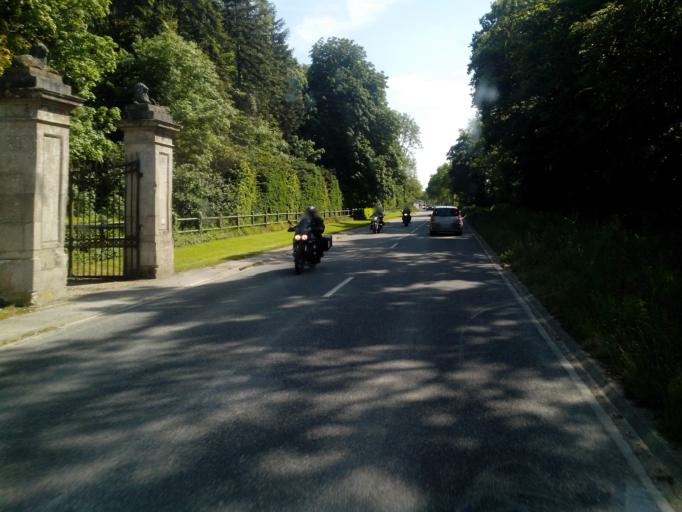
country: FR
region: Picardie
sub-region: Departement de la Somme
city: Quend
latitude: 50.3518
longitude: 1.6484
